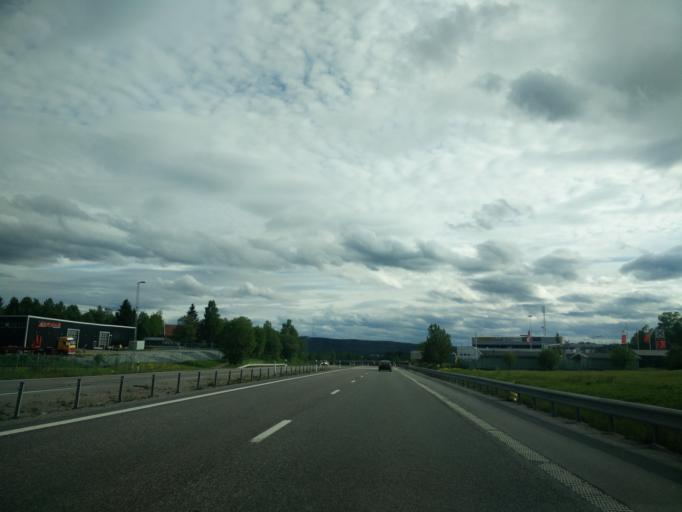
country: SE
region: Vaesternorrland
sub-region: Sundsvalls Kommun
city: Johannedal
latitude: 62.4170
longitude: 17.3442
